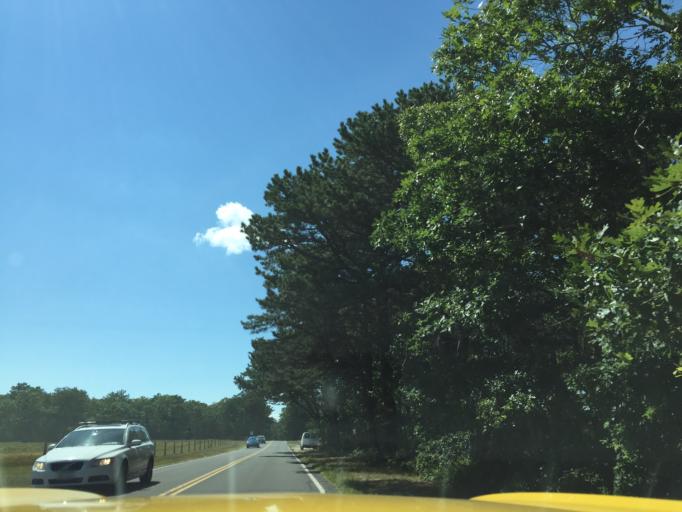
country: US
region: New York
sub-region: Suffolk County
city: Sag Harbor
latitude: 40.9635
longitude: -72.2507
